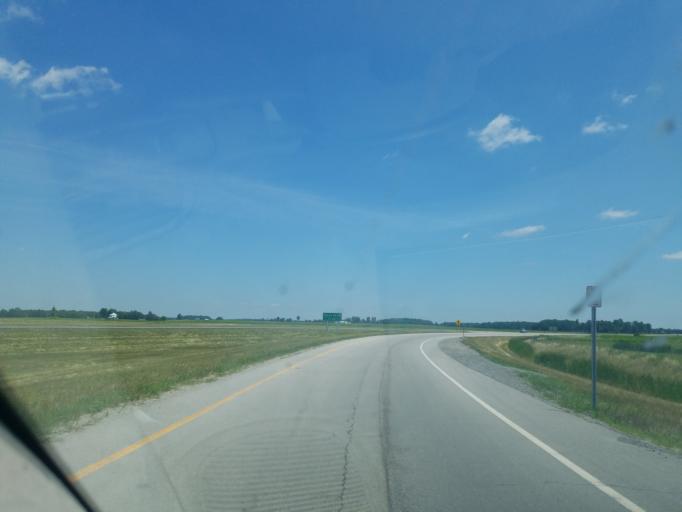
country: US
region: Ohio
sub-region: Hardin County
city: Forest
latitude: 40.8247
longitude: -83.5174
